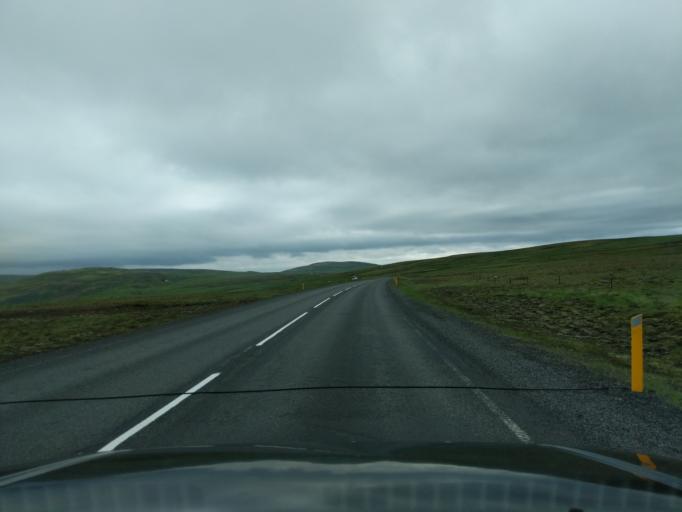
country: IS
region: Capital Region
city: Mosfellsbaer
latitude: 64.1960
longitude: -21.5086
